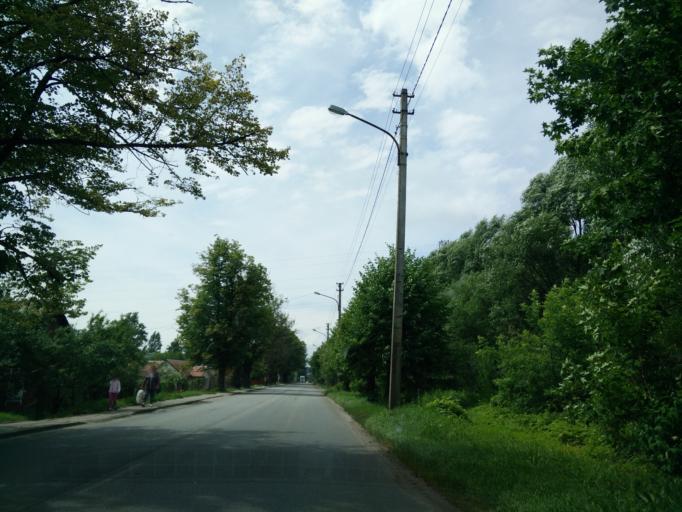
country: LT
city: Skaidiskes
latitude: 54.6944
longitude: 25.4460
